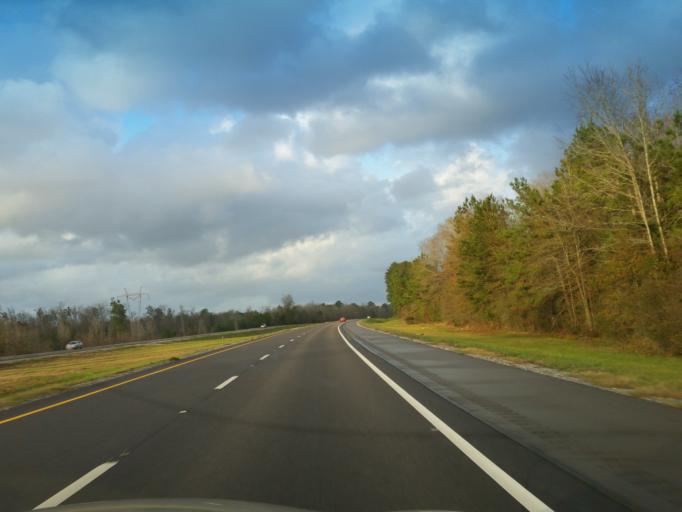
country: US
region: Mississippi
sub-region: Jones County
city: Sharon
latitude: 31.9205
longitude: -89.0044
